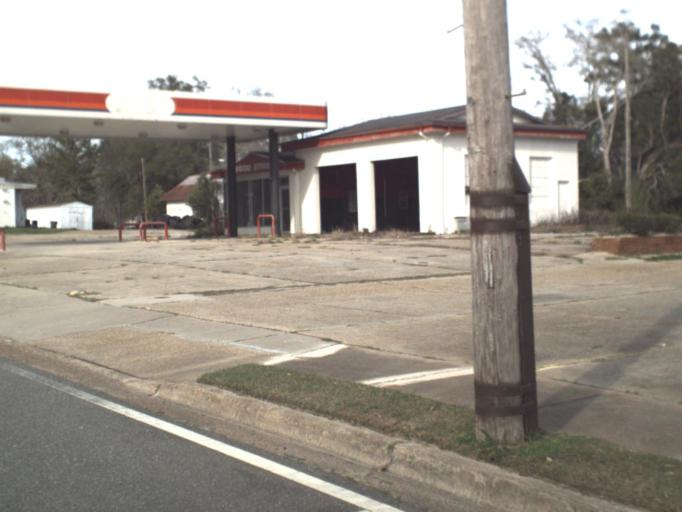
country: US
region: Florida
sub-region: Jefferson County
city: Monticello
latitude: 30.5558
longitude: -83.8701
